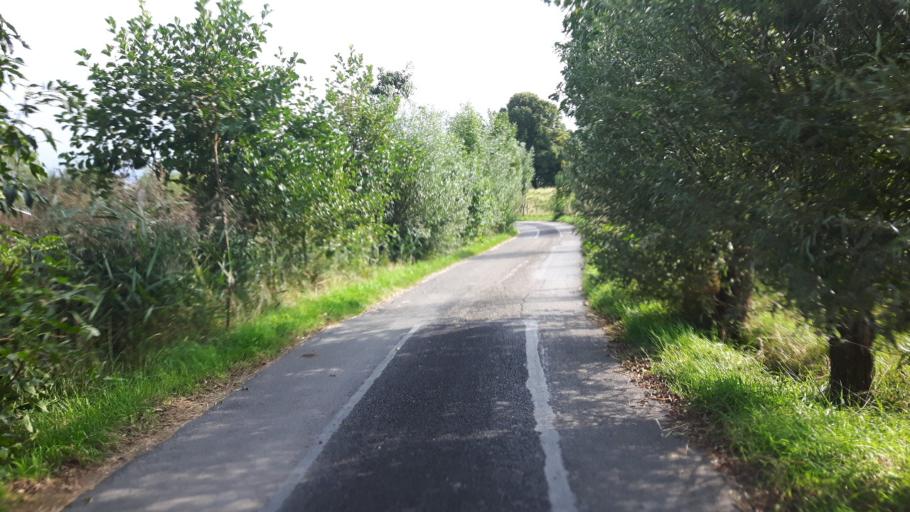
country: NL
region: North Holland
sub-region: Gemeente Ouder-Amstel
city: Ouderkerk aan de Amstel
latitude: 52.2710
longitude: 4.9286
